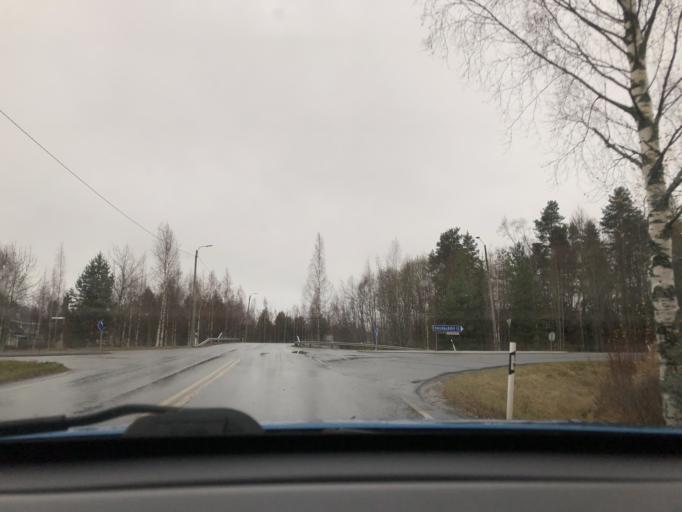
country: FI
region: Pirkanmaa
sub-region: Tampere
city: Kangasala
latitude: 61.4538
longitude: 24.0349
